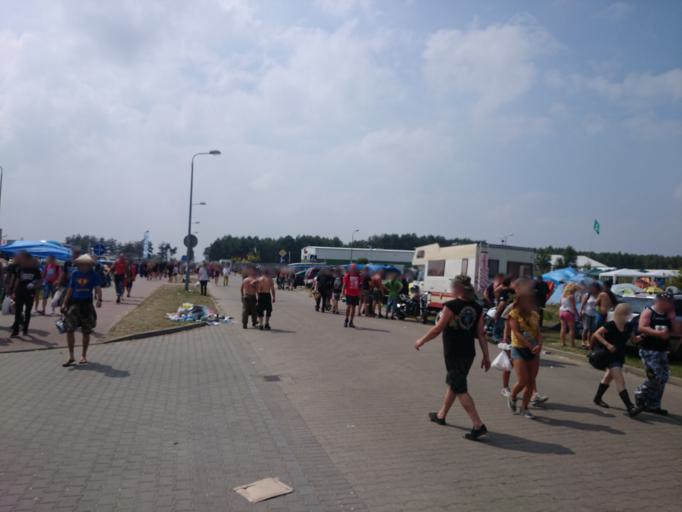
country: PL
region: Lubusz
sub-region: Powiat gorzowski
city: Kostrzyn nad Odra
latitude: 52.6061
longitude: 14.6750
